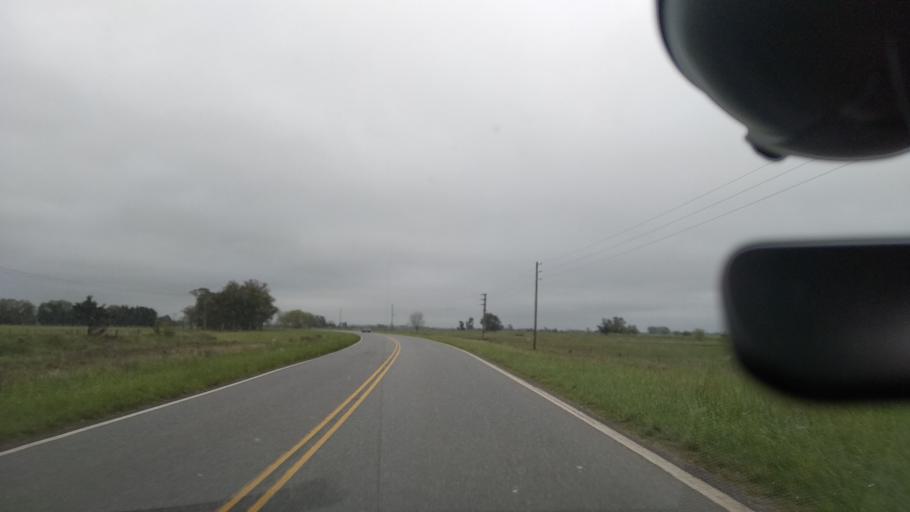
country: AR
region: Buenos Aires
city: Veronica
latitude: -35.3020
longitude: -57.5029
